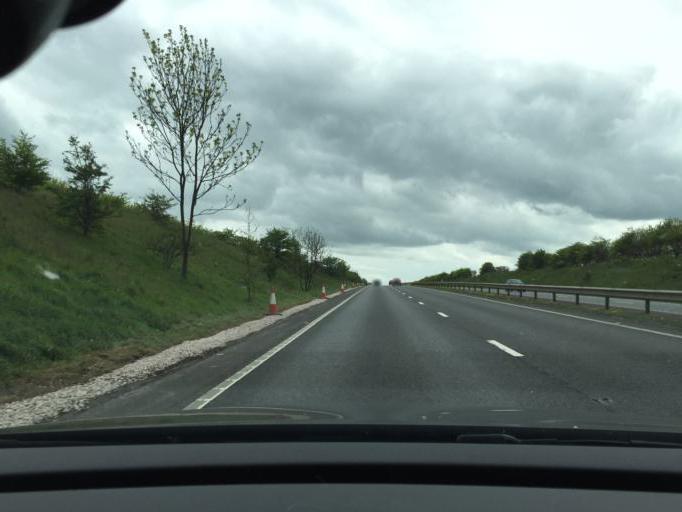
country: GB
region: England
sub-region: Oxfordshire
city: Harwell
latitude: 51.5867
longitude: -1.2840
